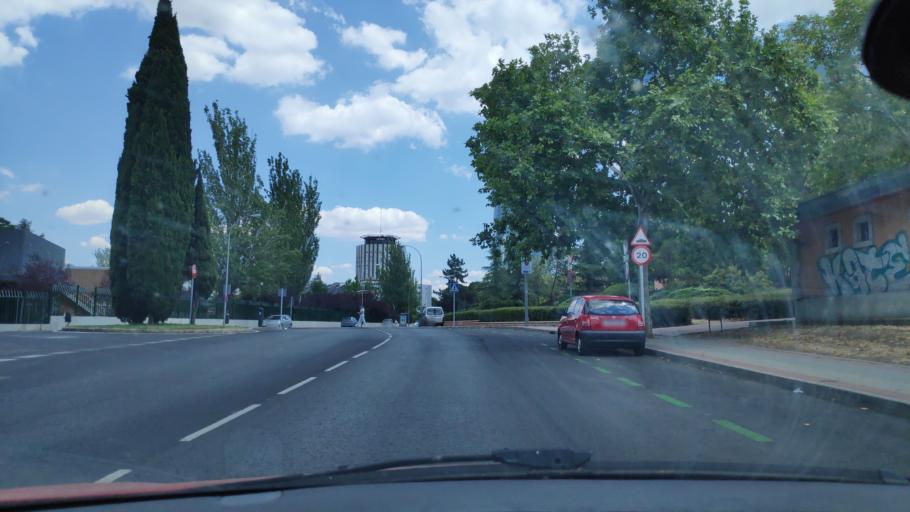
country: ES
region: Madrid
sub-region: Provincia de Madrid
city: Pinar de Chamartin
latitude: 40.4813
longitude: -3.6930
